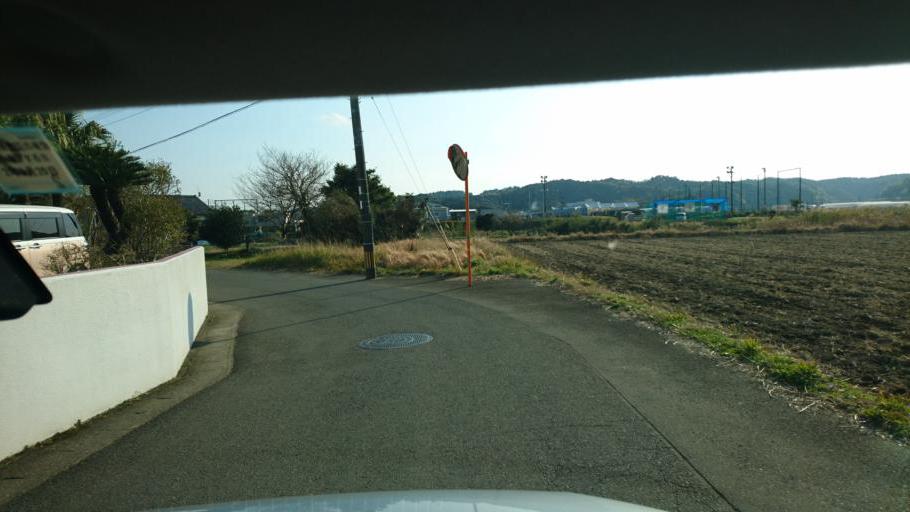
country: JP
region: Miyazaki
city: Miyazaki-shi
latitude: 32.0056
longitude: 131.4394
